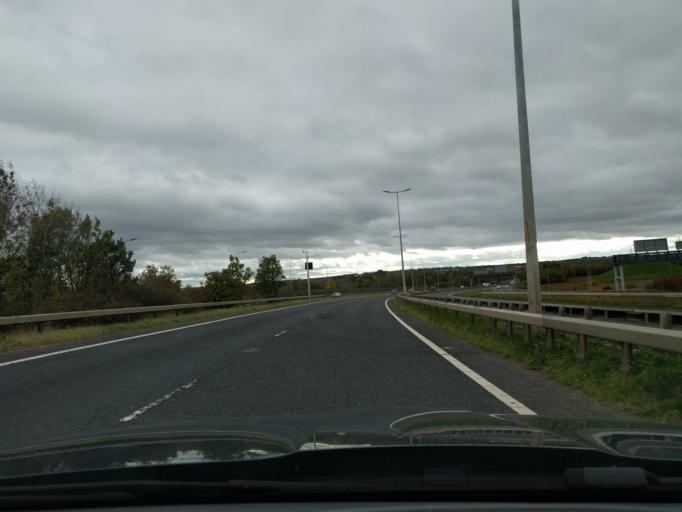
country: GB
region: England
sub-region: Newcastle upon Tyne
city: Hazlerigg
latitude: 55.0333
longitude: -1.6295
